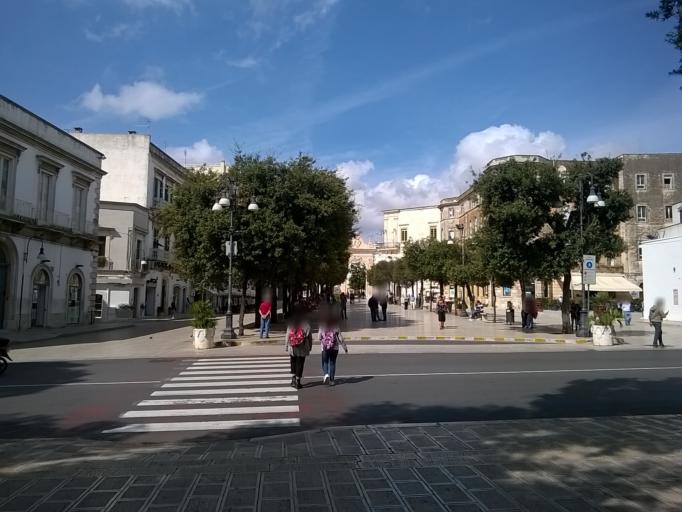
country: IT
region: Apulia
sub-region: Provincia di Taranto
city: Martina Franca
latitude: 40.7041
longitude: 17.3401
